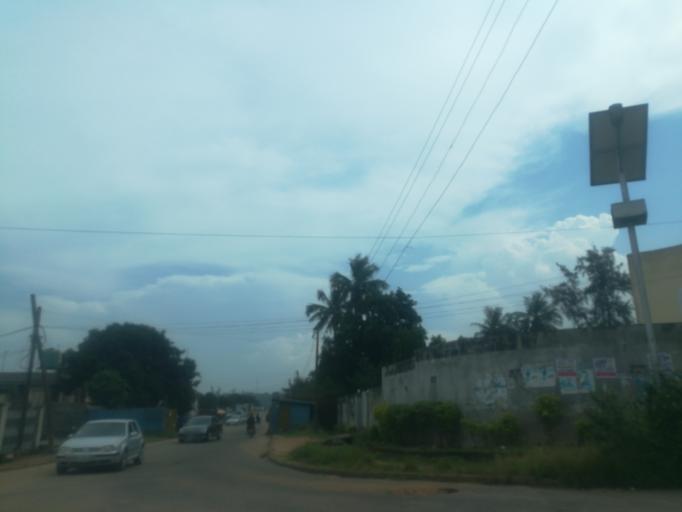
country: NG
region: Oyo
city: Ibadan
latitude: 7.4234
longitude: 3.9142
